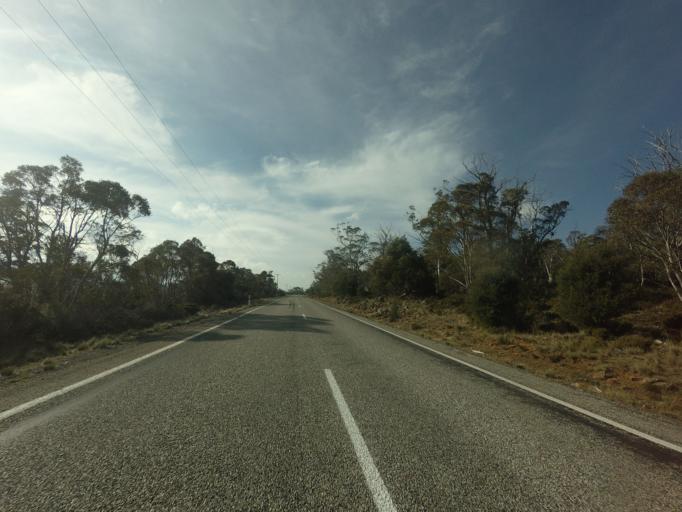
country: AU
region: Tasmania
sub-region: Meander Valley
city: Deloraine
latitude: -41.9889
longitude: 146.7096
